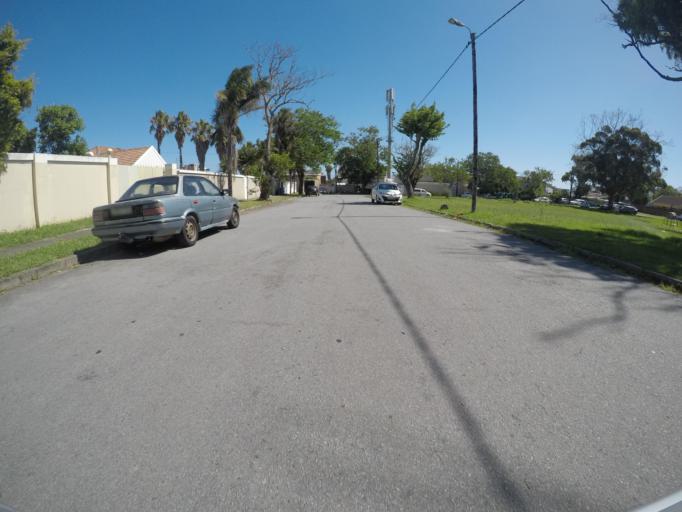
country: ZA
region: Eastern Cape
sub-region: Buffalo City Metropolitan Municipality
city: East London
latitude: -32.9848
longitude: 27.9278
